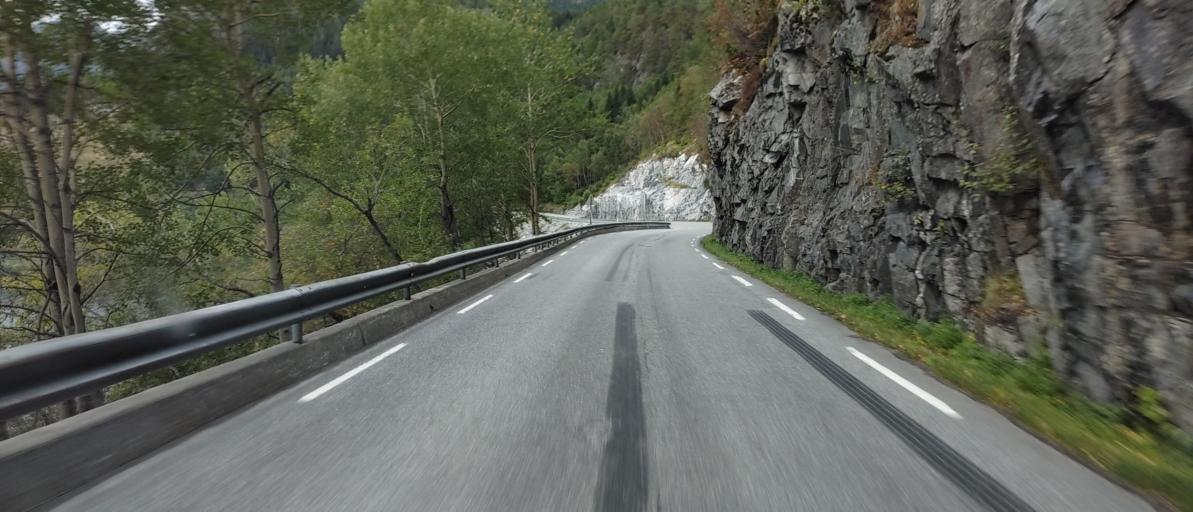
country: NO
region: More og Romsdal
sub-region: Rauma
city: Andalsnes
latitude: 62.5784
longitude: 7.5397
